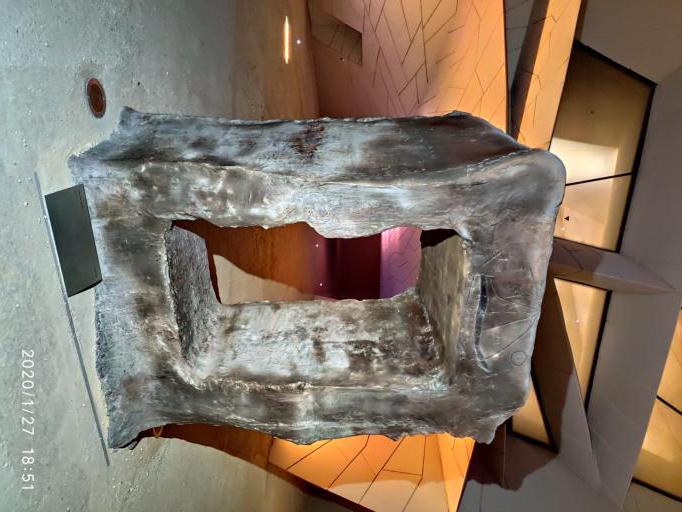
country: QA
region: Baladiyat ad Dawhah
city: Doha
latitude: 25.2867
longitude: 51.5493
